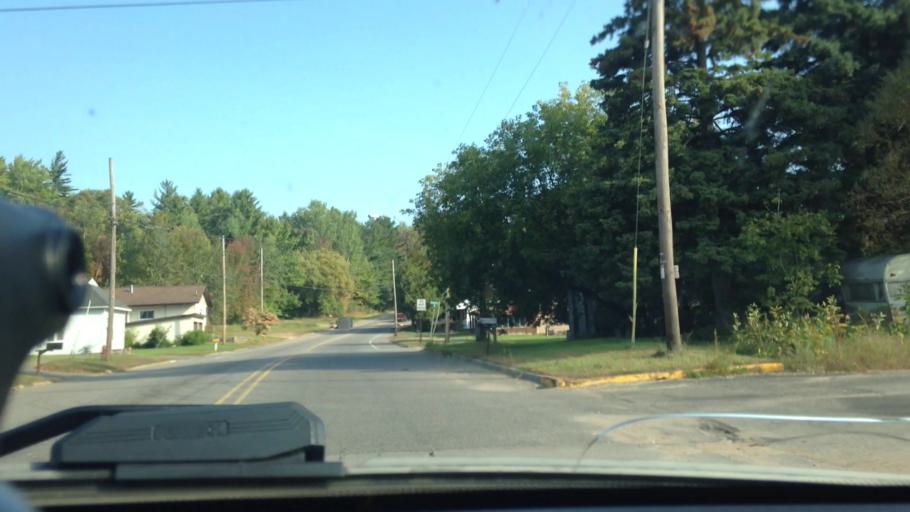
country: US
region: Michigan
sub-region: Dickinson County
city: Quinnesec
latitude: 45.8070
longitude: -87.9884
